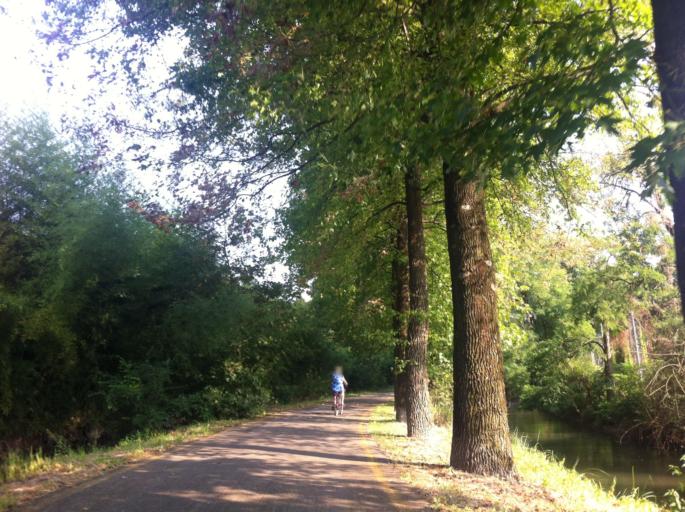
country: IT
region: Lombardy
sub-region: Provincia di Lodi
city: Casalmaiocco
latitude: 45.3508
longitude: 9.3690
